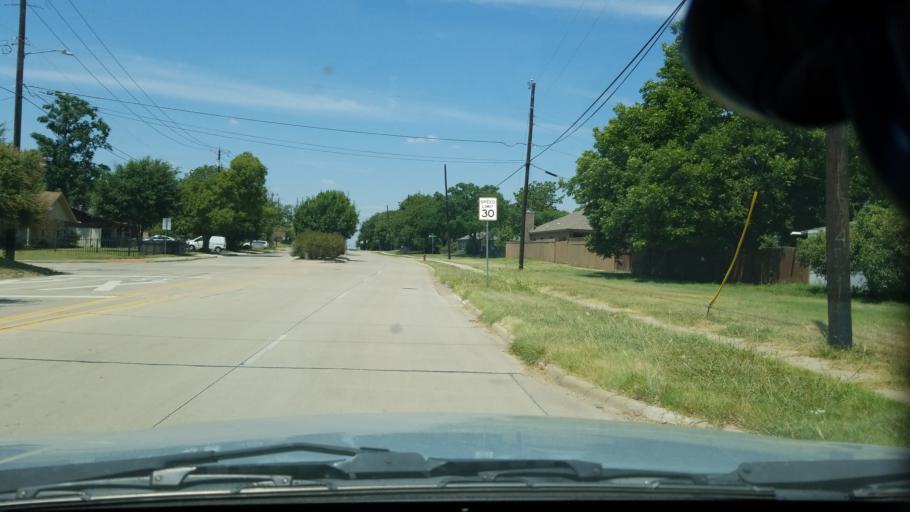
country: US
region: Texas
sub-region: Dallas County
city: Grand Prairie
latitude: 32.7602
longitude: -96.9565
